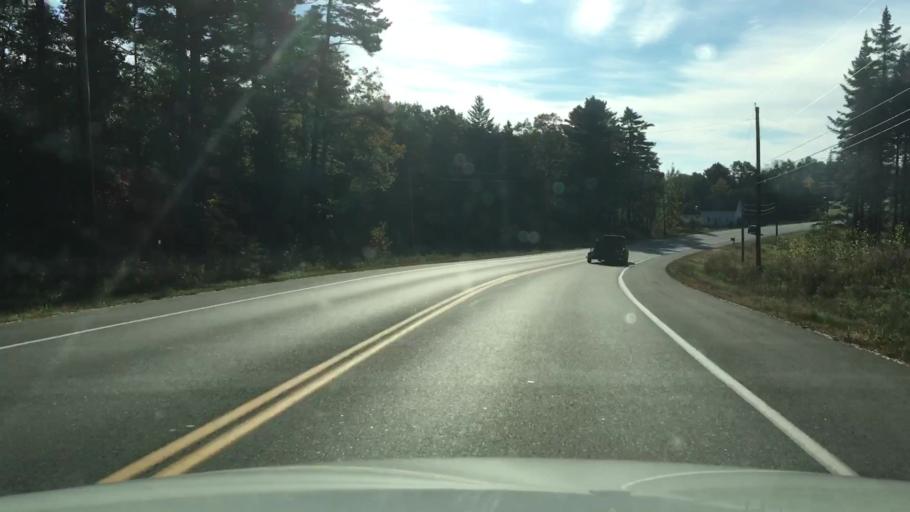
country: US
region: Maine
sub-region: Knox County
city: Warren
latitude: 44.0901
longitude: -69.2348
